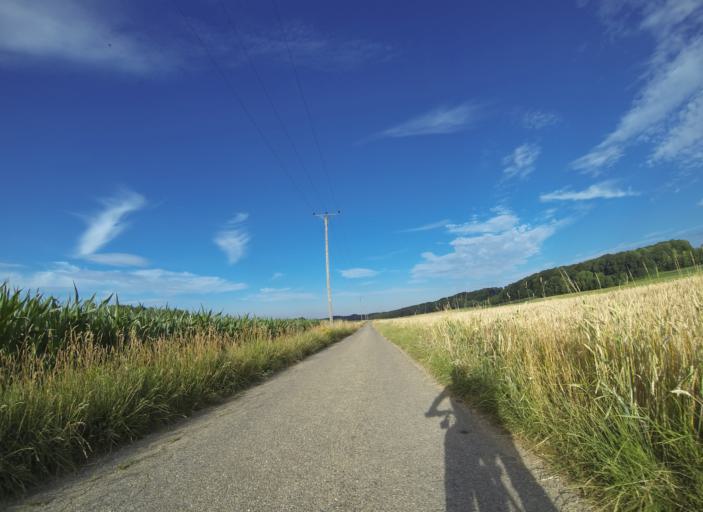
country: DE
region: Baden-Wuerttemberg
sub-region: Tuebingen Region
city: Altheim
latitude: 48.3253
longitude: 9.7782
